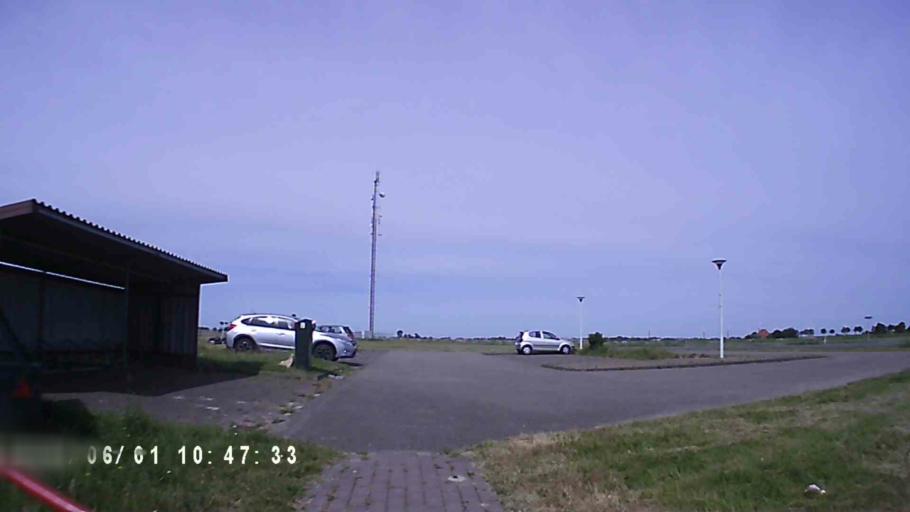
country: NL
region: Friesland
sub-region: Gemeente Franekeradeel
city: Franeker
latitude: 53.2014
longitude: 5.5399
